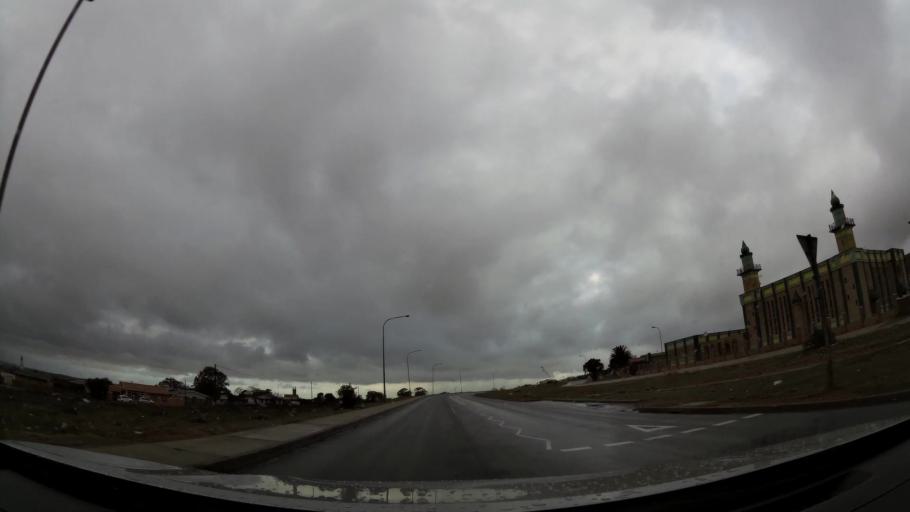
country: ZA
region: Eastern Cape
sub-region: Nelson Mandela Bay Metropolitan Municipality
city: Port Elizabeth
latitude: -33.8880
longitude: 25.5176
